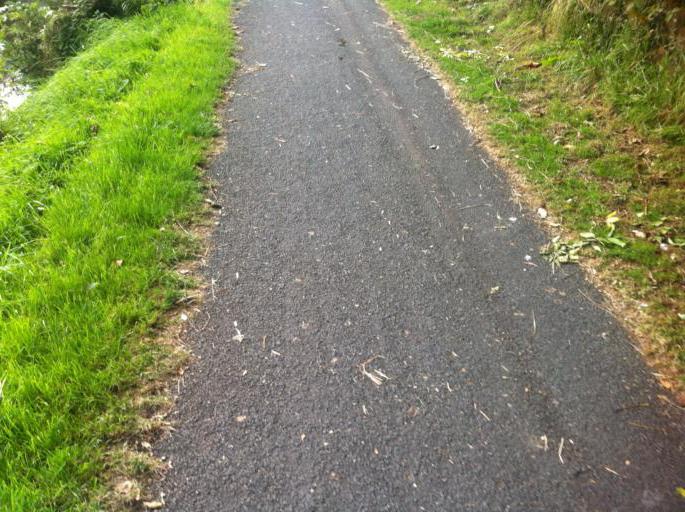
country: GB
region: Scotland
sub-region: East Dunbartonshire
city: Kirkintilloch
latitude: 55.9369
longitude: -4.1567
